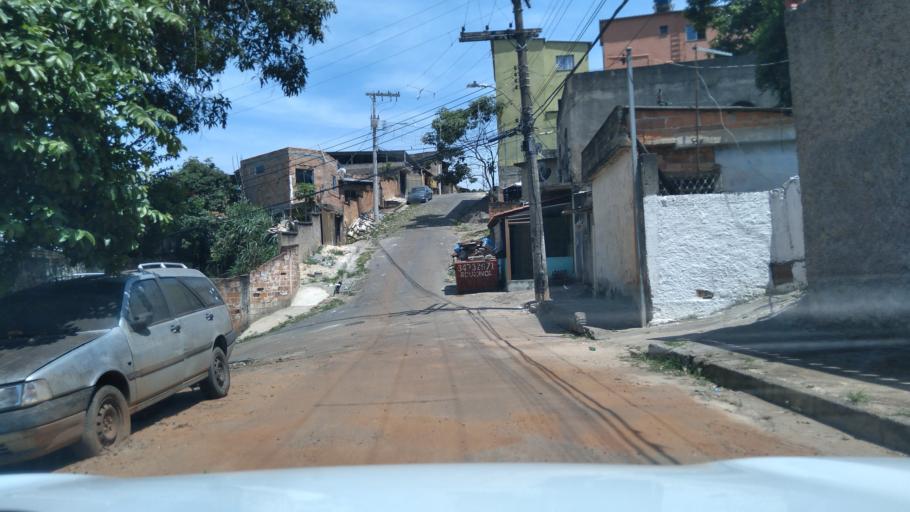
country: BR
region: Minas Gerais
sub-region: Contagem
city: Contagem
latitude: -19.9169
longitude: -44.0214
